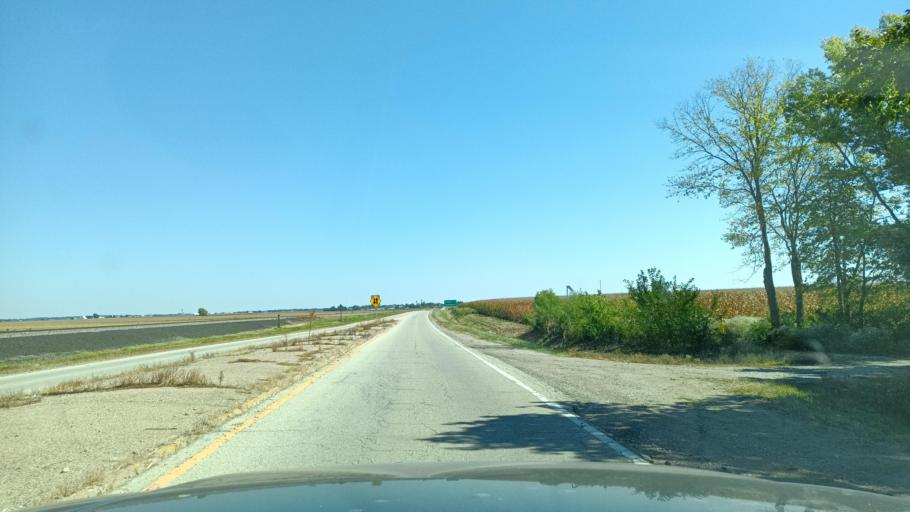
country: US
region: Illinois
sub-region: Tazewell County
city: Mackinaw
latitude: 40.6266
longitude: -89.3272
